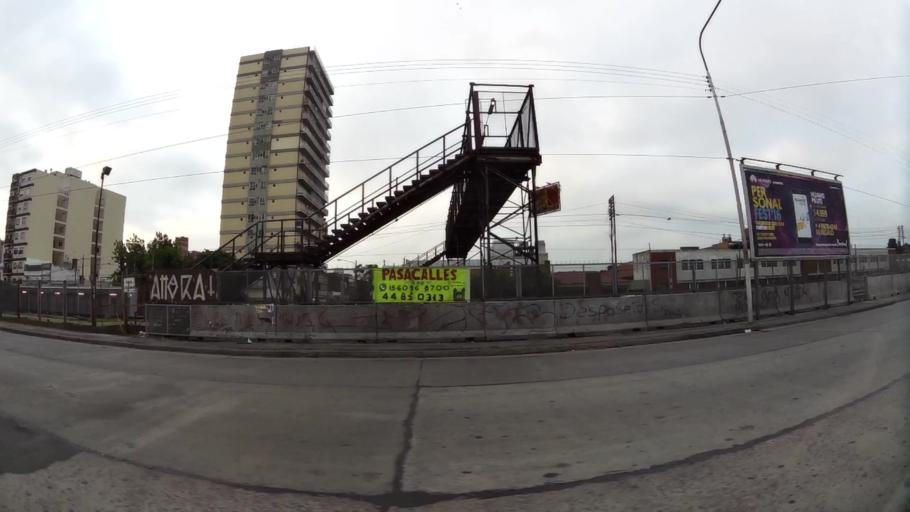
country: AR
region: Buenos Aires
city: San Justo
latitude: -34.6401
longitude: -58.5391
